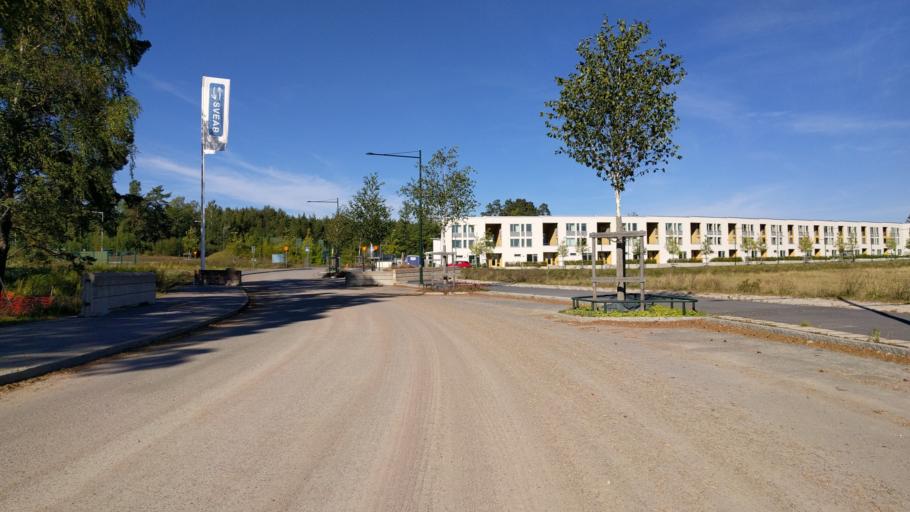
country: SE
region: Stockholm
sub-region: Taby Kommun
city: Taby
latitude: 59.4712
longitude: 18.1190
